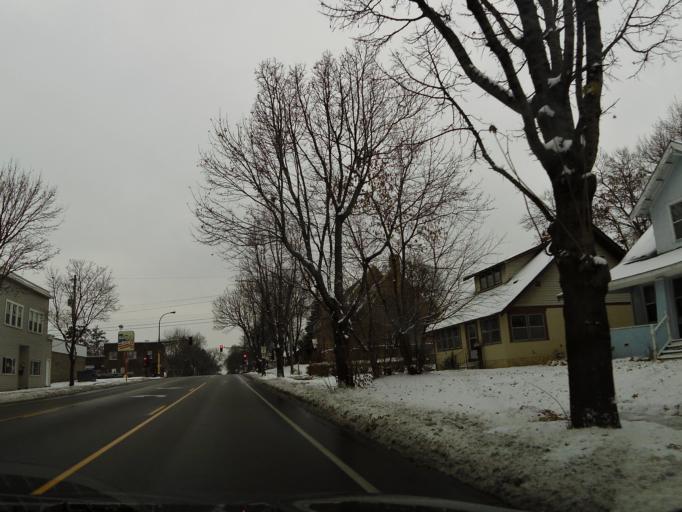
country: US
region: Minnesota
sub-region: Ramsey County
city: Saint Paul
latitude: 44.9776
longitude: -93.0544
